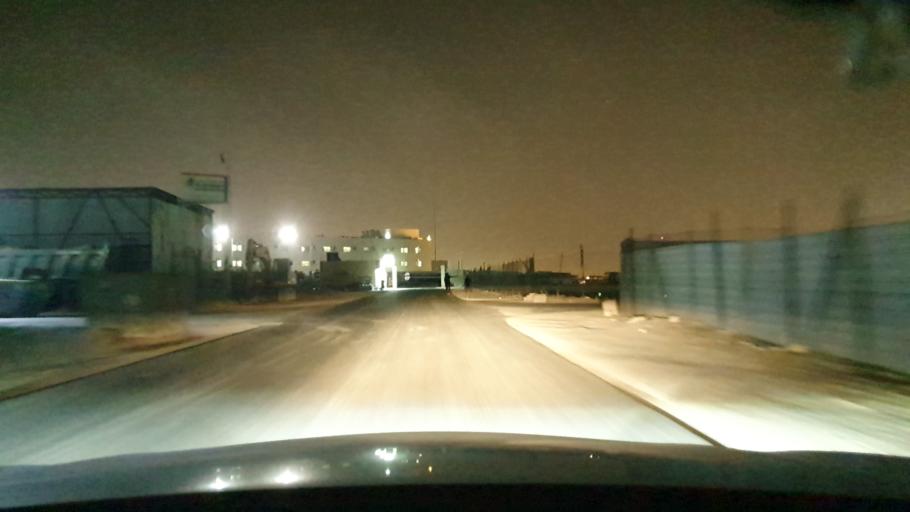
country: BH
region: Northern
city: Sitrah
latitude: 26.0973
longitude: 50.6162
